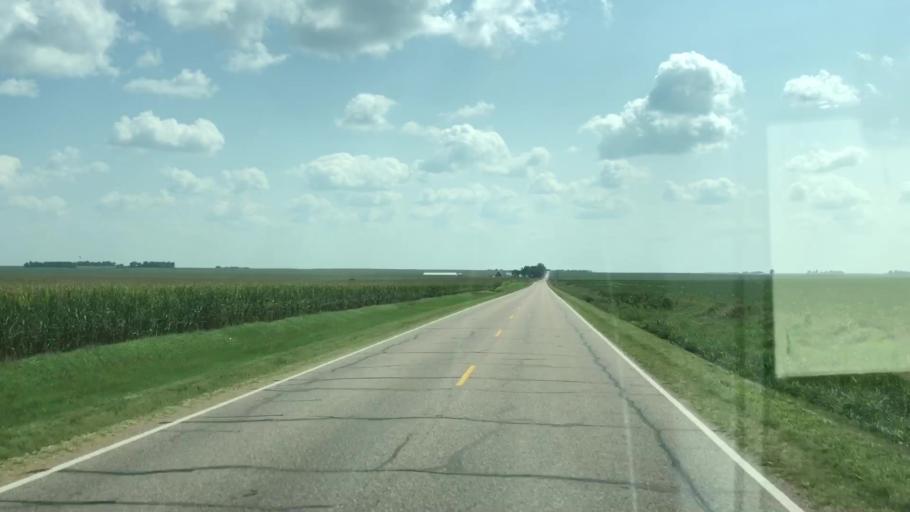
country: US
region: Iowa
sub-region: O'Brien County
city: Sheldon
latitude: 43.1640
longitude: -95.8019
